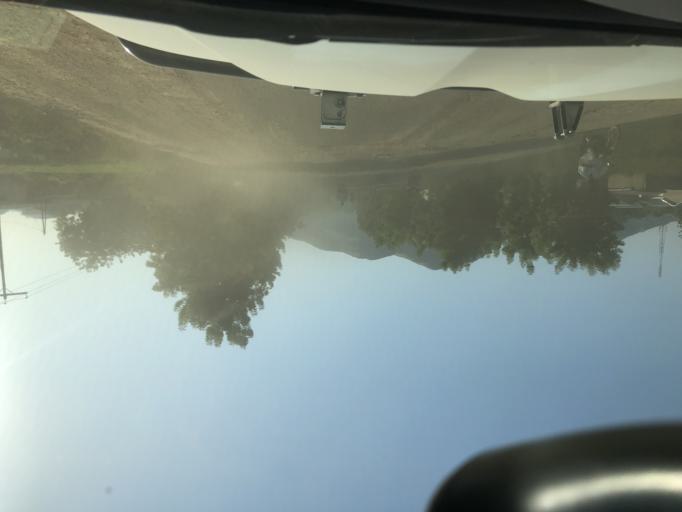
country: CM
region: Far North
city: Maroua
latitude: 10.5994
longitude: 14.2960
